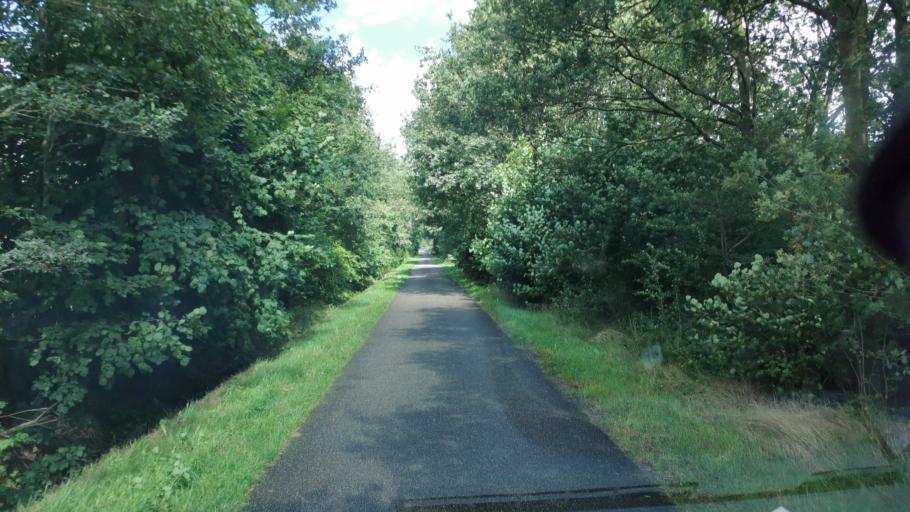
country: NL
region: Overijssel
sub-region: Gemeente Haaksbergen
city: Haaksbergen
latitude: 52.1364
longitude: 6.7418
